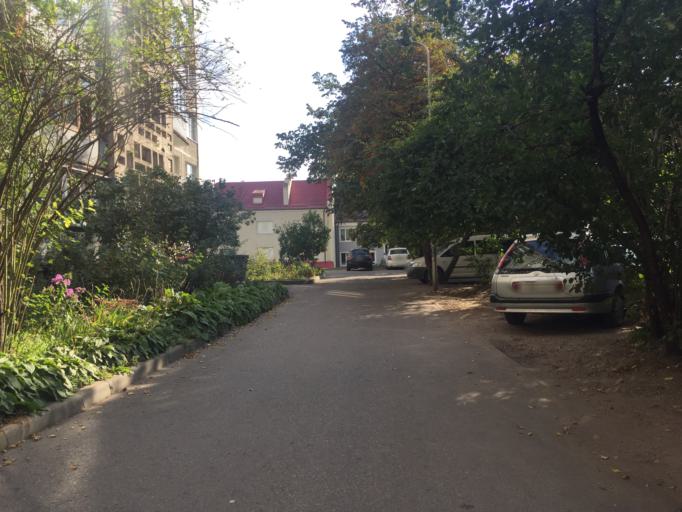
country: RU
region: Kaliningrad
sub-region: Gorod Kaliningrad
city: Kaliningrad
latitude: 54.6965
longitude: 20.5088
